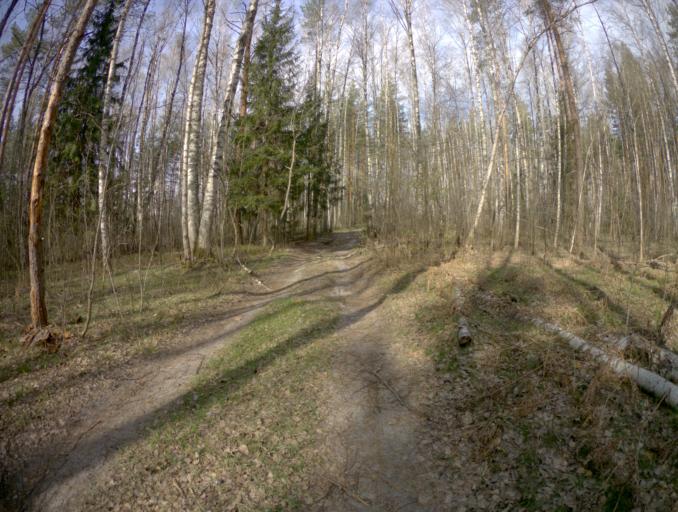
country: RU
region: Vladimir
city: Mezinovskiy
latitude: 55.6020
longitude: 40.3910
